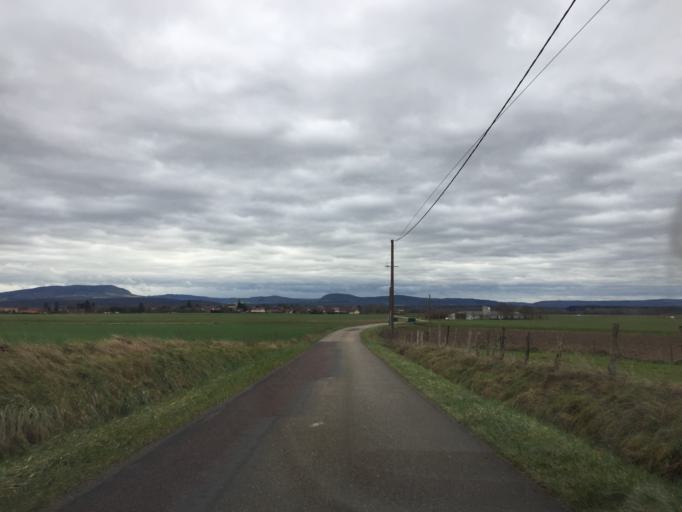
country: FR
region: Franche-Comte
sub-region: Departement du Doubs
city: Arc-et-Senans
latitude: 47.0280
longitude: 5.7073
